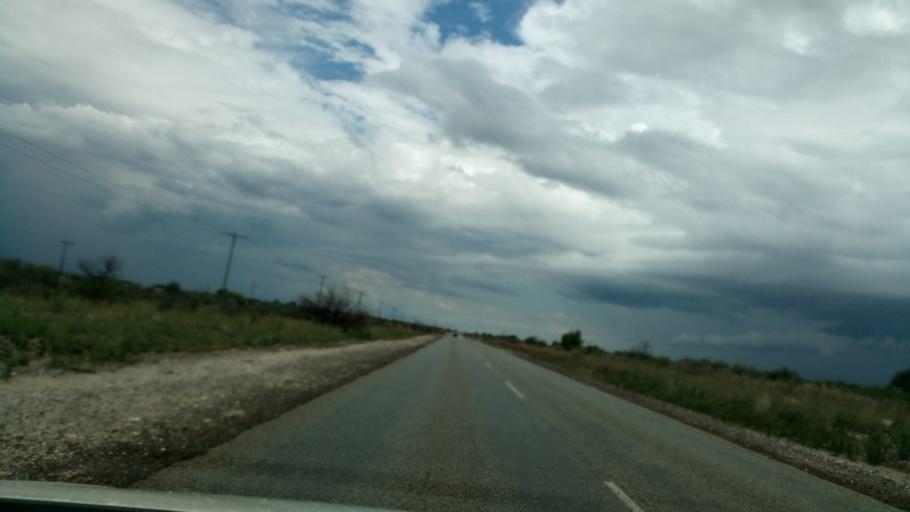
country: ZA
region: Northern Cape
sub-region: Siyanda District Municipality
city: Danielskuil
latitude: -28.2554
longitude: 24.0481
